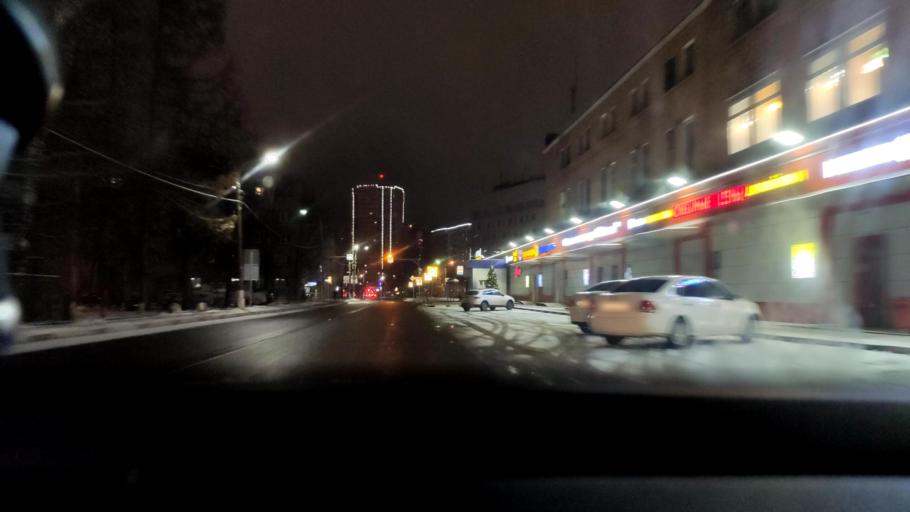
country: RU
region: Moskovskaya
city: Solnechnogorsk
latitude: 56.1830
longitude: 36.9773
